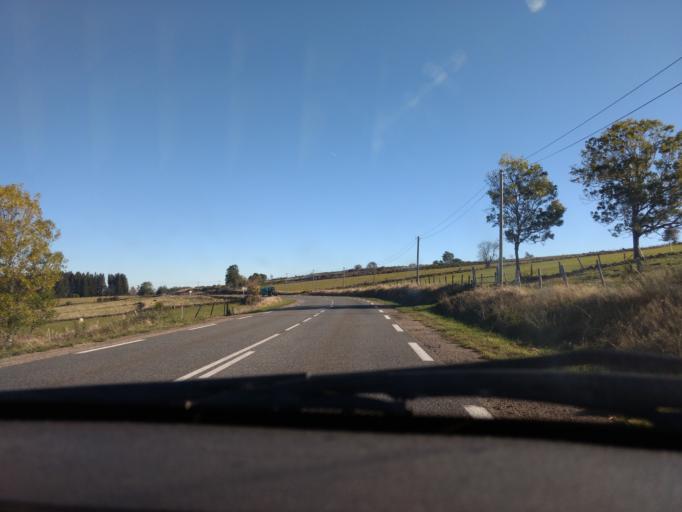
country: FR
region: Midi-Pyrenees
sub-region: Departement de l'Aveyron
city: Laguiole
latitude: 44.7513
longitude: 2.8720
